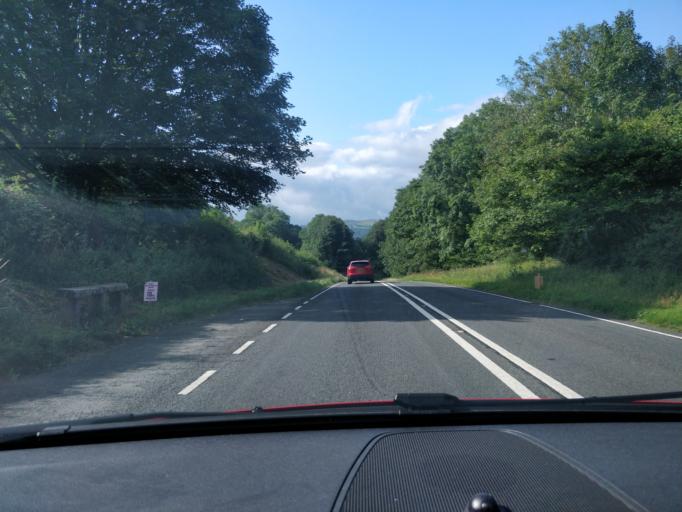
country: GB
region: Wales
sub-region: Conwy
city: Llansantffraid Glan Conwy
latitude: 53.2160
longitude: -3.8248
